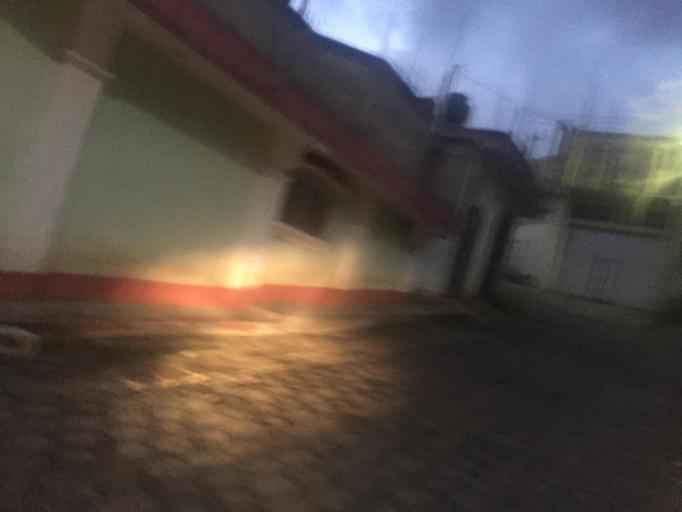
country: GT
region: Totonicapan
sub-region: Municipio de Totonicapan
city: Totonicapan
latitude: 14.9171
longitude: -91.3578
